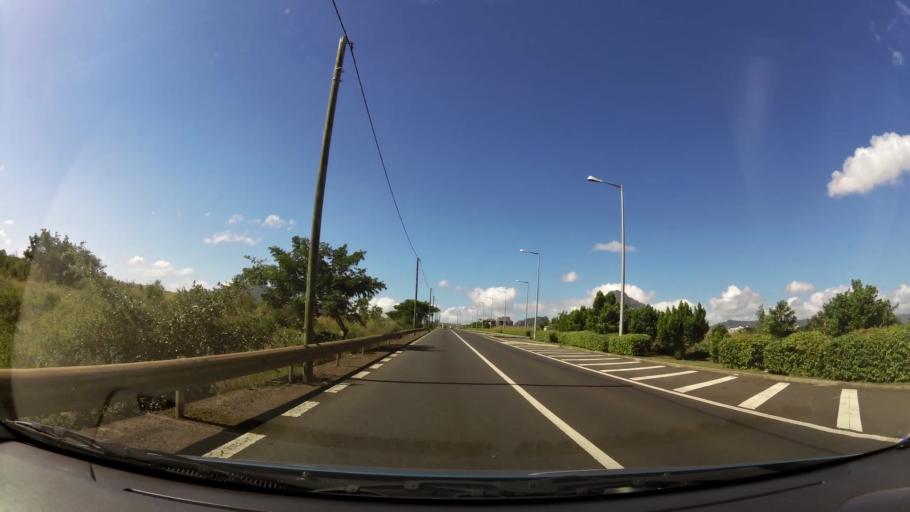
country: MU
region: Black River
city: Flic en Flac
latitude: -20.2770
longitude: 57.3826
